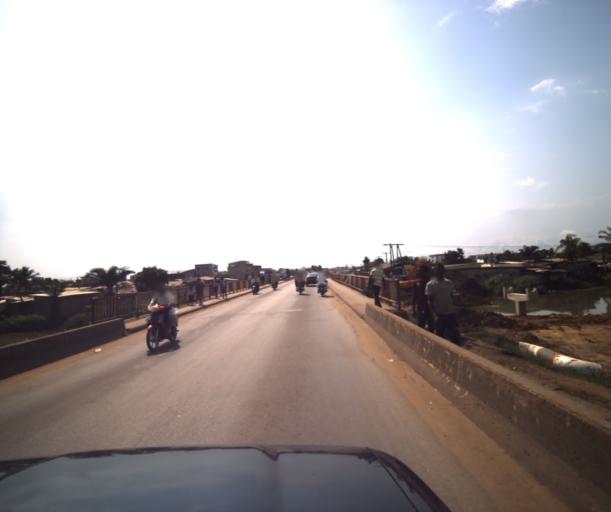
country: CM
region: Littoral
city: Douala
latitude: 4.0096
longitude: 9.7386
